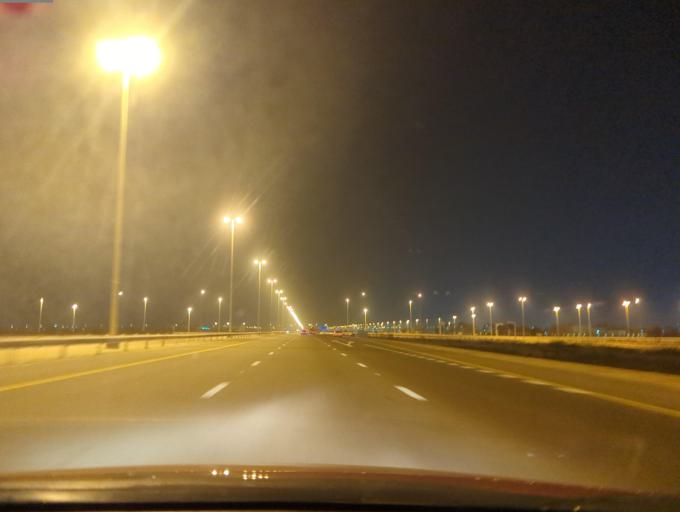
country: AE
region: Abu Dhabi
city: Abu Dhabi
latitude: 24.4031
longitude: 54.7531
